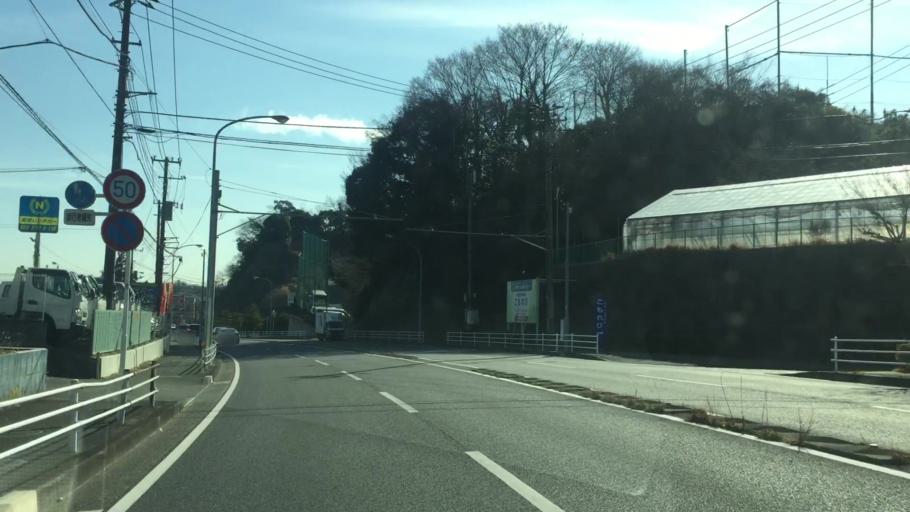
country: JP
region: Kanagawa
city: Zushi
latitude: 35.3511
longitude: 139.6070
